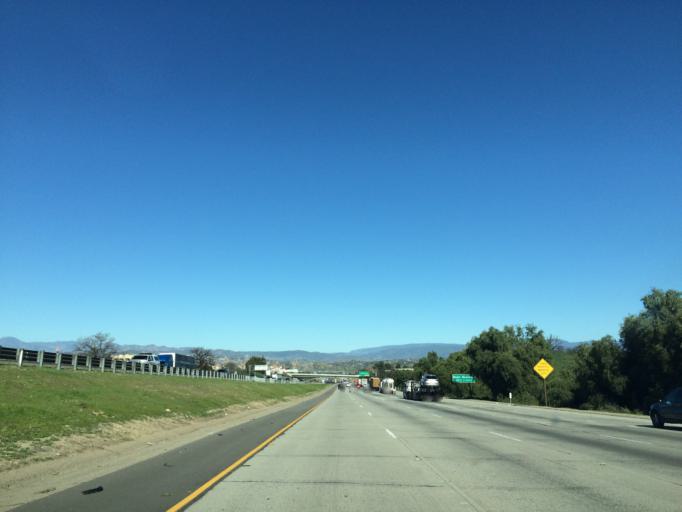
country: US
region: California
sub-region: Los Angeles County
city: Santa Clarita
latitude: 34.4014
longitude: -118.5731
